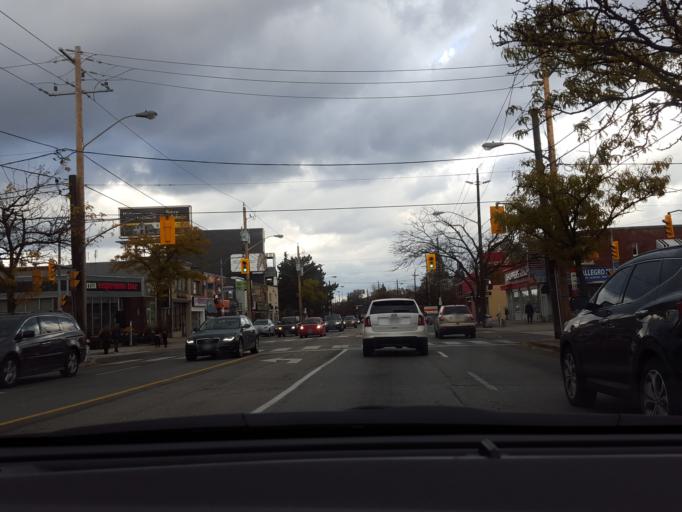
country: CA
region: Ontario
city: North York
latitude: 43.7355
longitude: -79.4200
